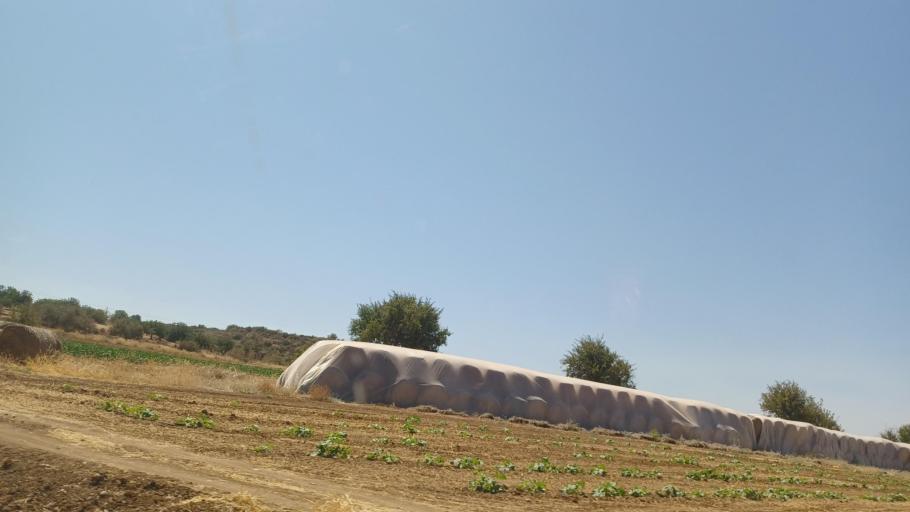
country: CY
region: Pafos
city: Polis
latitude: 35.0532
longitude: 32.4688
